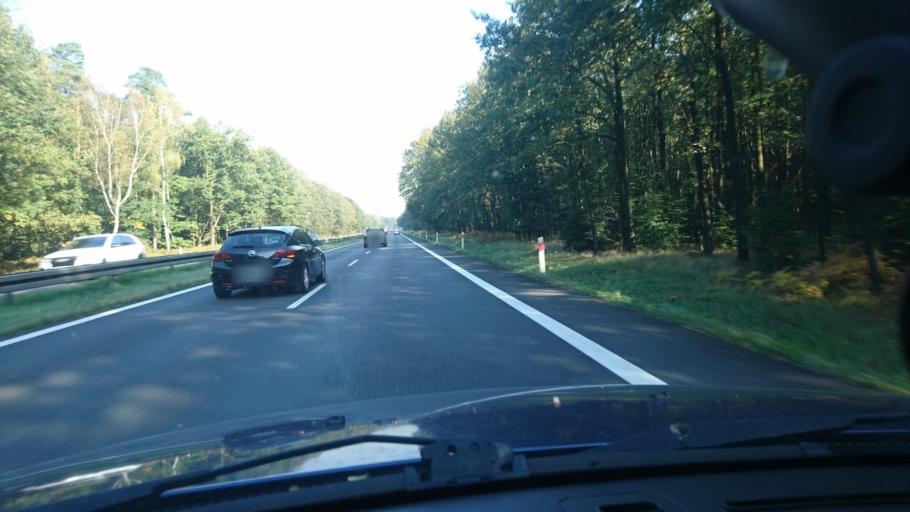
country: PL
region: Silesian Voivodeship
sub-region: Powiat pszczynski
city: Kobior
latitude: 50.0408
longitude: 18.9421
